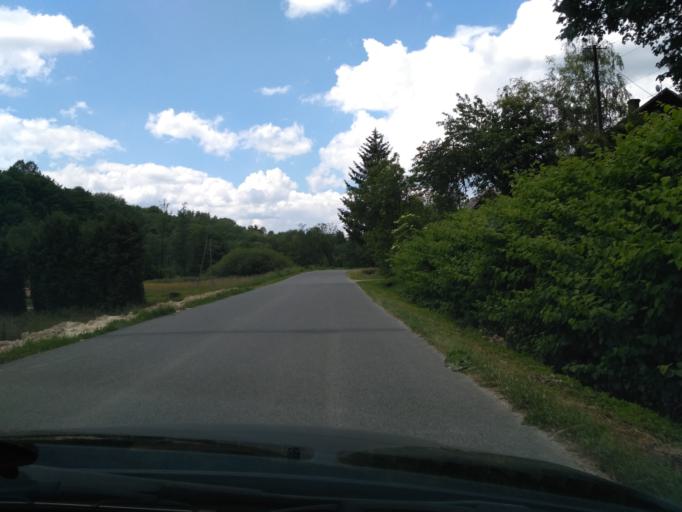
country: PL
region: Subcarpathian Voivodeship
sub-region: Powiat brzozowski
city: Golcowa
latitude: 49.8102
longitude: 22.0535
